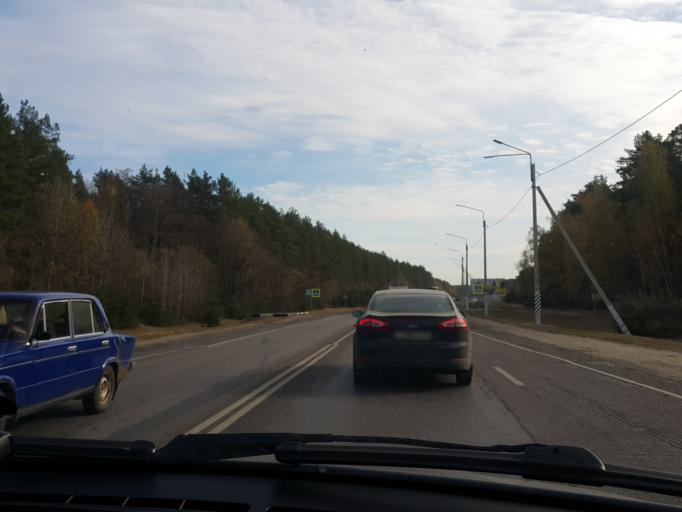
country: RU
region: Tambov
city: Donskoye
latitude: 52.7139
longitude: 41.5170
